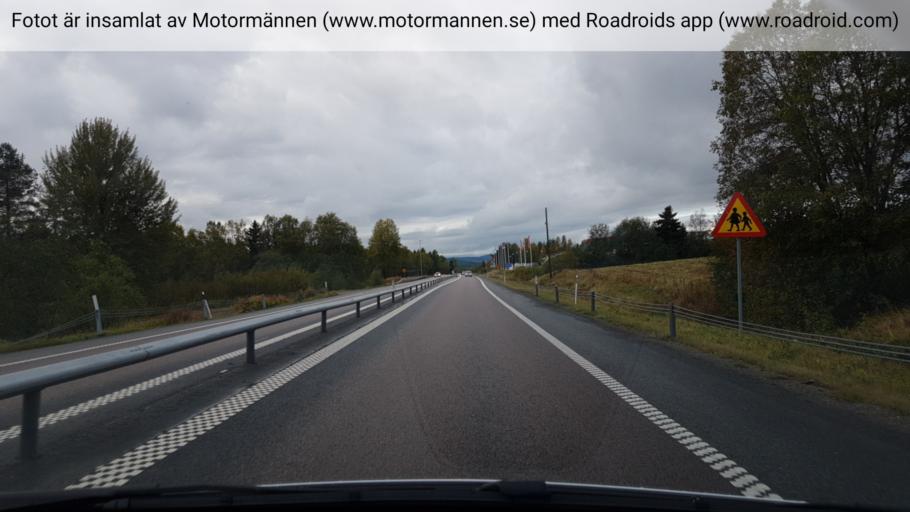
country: SE
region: Vaesternorrland
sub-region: OErnskoeldsviks Kommun
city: Ornskoldsvik
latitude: 63.3014
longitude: 18.9043
